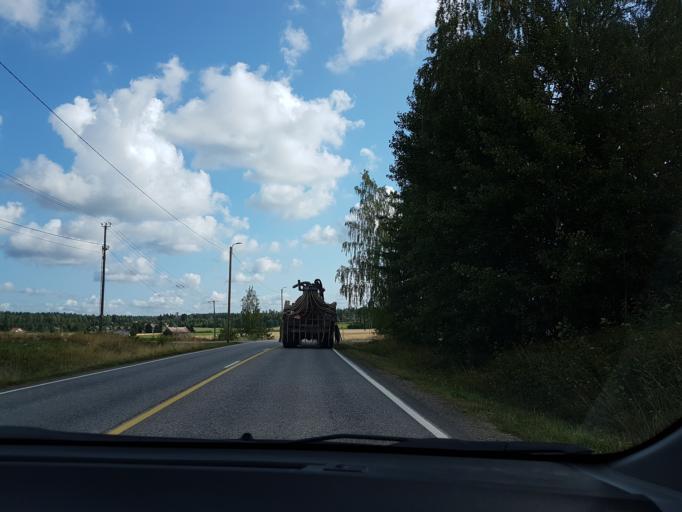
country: FI
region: Uusimaa
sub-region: Helsinki
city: Pornainen
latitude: 60.4846
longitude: 25.3460
